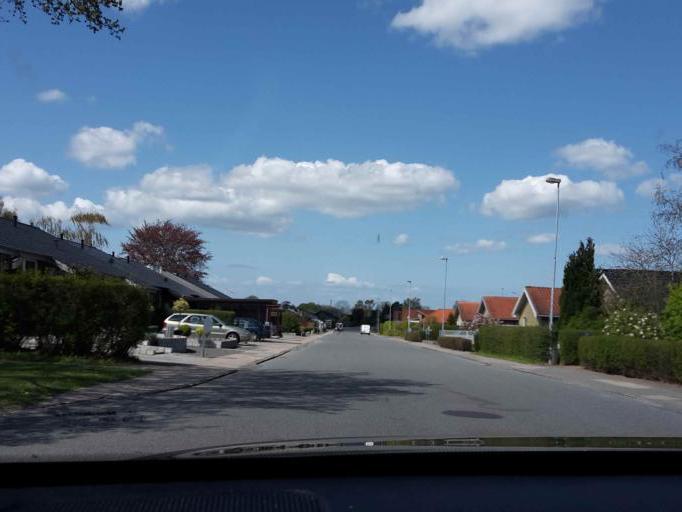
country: DK
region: South Denmark
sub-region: Odense Kommune
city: Odense
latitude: 55.4137
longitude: 10.3293
